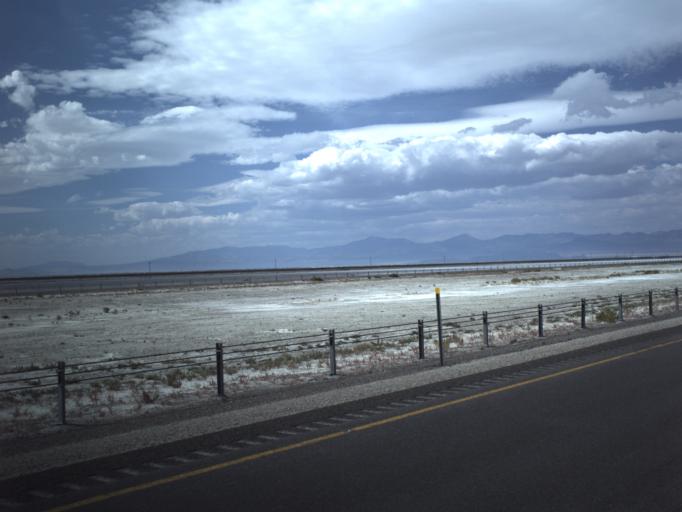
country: US
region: Utah
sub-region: Tooele County
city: Wendover
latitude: 40.7389
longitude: -113.8248
